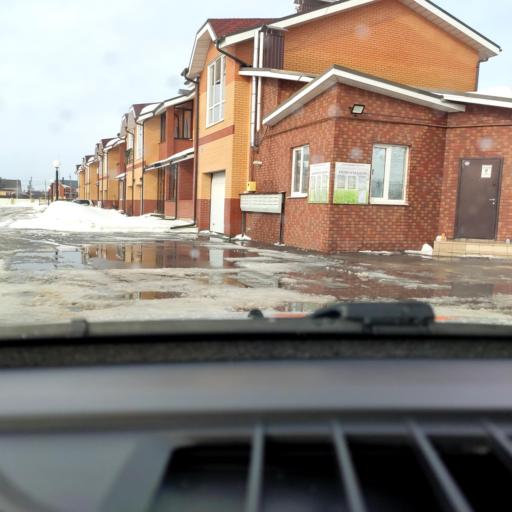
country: RU
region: Voronezj
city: Podgornoye
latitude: 51.7712
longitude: 39.1260
